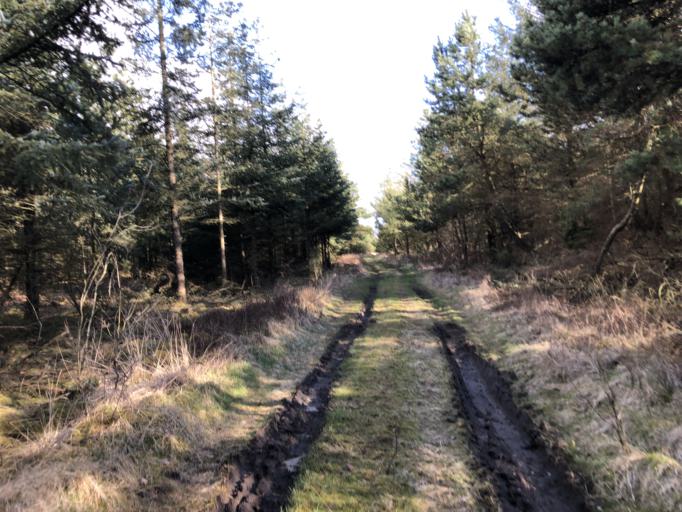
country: DK
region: Central Jutland
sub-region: Holstebro Kommune
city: Ulfborg
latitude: 56.2747
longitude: 8.3502
